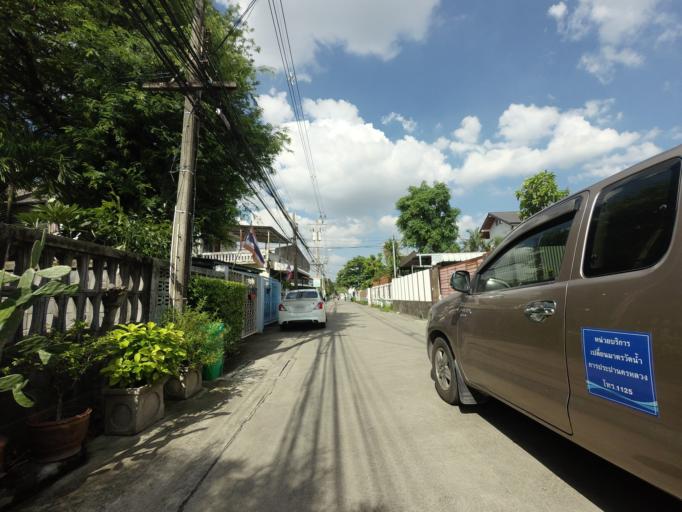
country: TH
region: Bangkok
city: Wang Thonglang
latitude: 13.7874
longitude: 100.5962
